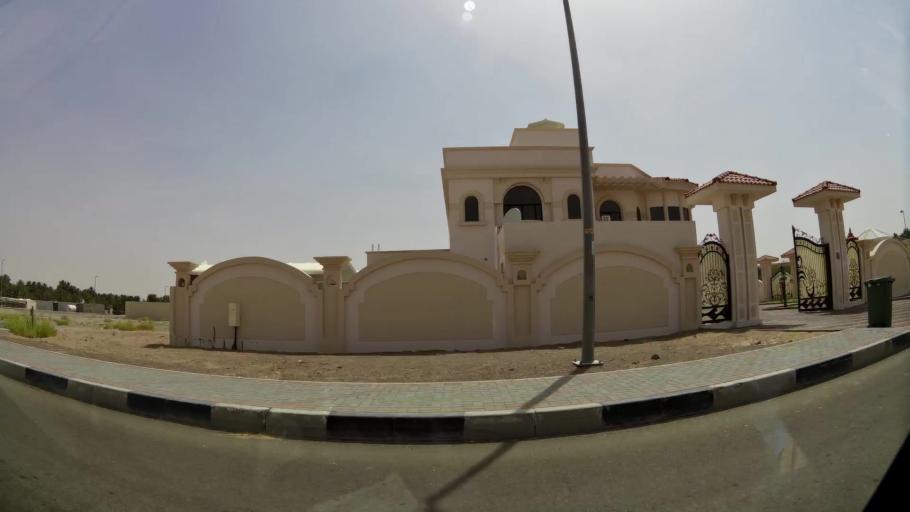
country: AE
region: Abu Dhabi
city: Al Ain
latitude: 24.1469
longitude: 55.6484
